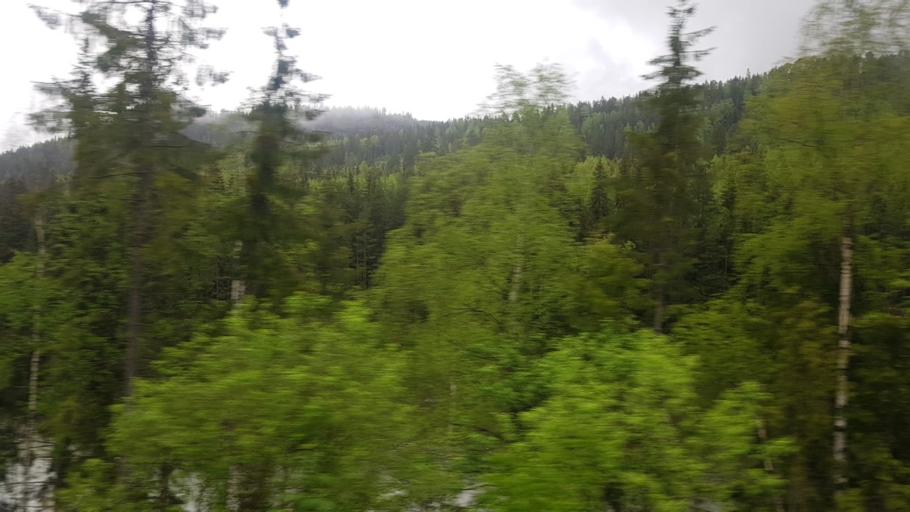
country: NO
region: Oppland
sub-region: Oyer
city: Tretten
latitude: 61.2768
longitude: 10.3597
